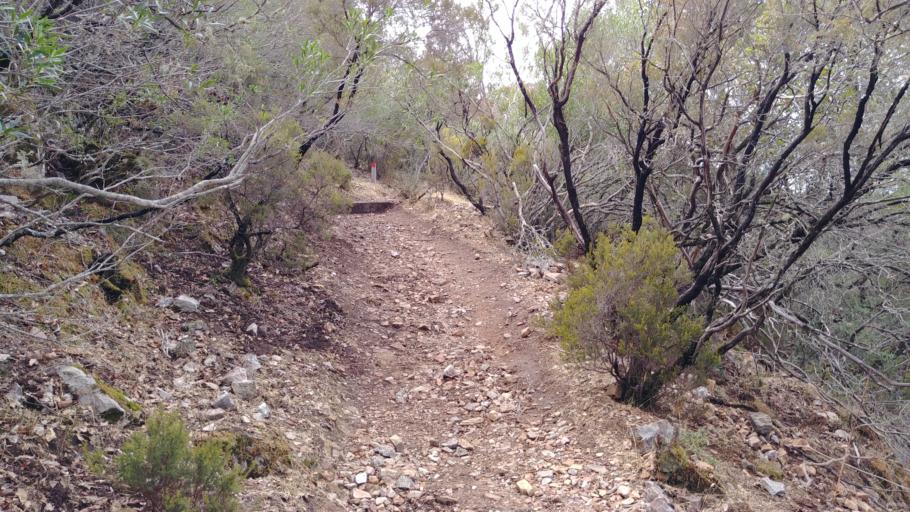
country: ES
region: Extremadura
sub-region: Provincia de Caceres
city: Torrejon el Rubio
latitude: 39.8295
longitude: -6.0395
